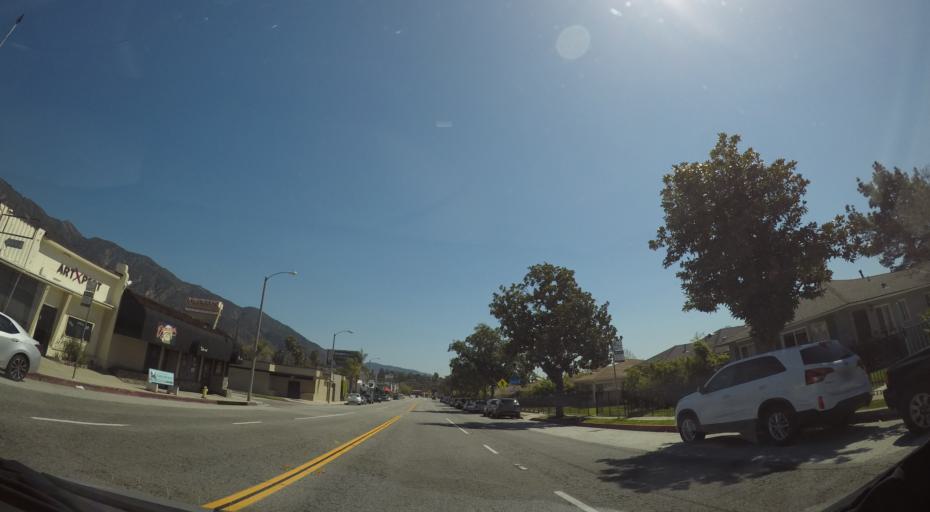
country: US
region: California
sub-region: Los Angeles County
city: East Pasadena
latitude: 34.1691
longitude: -118.1010
